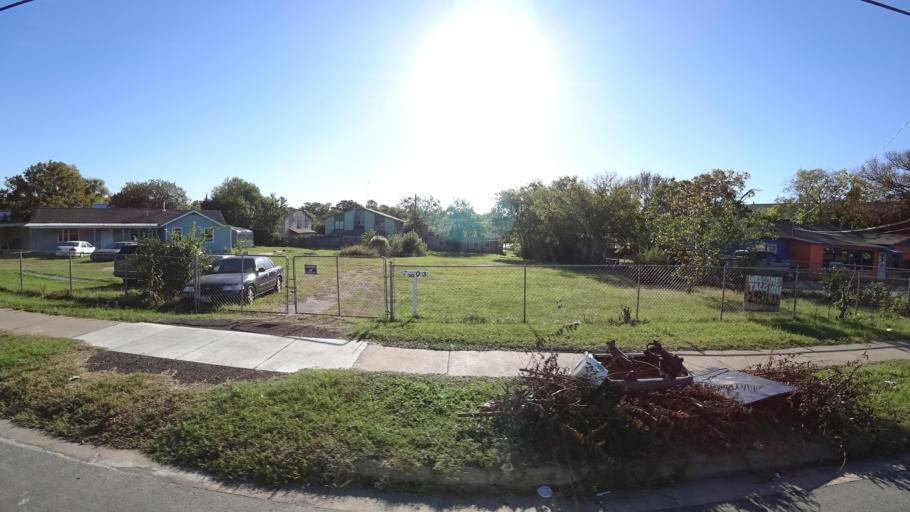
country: US
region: Texas
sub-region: Travis County
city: Austin
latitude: 30.3056
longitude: -97.6805
